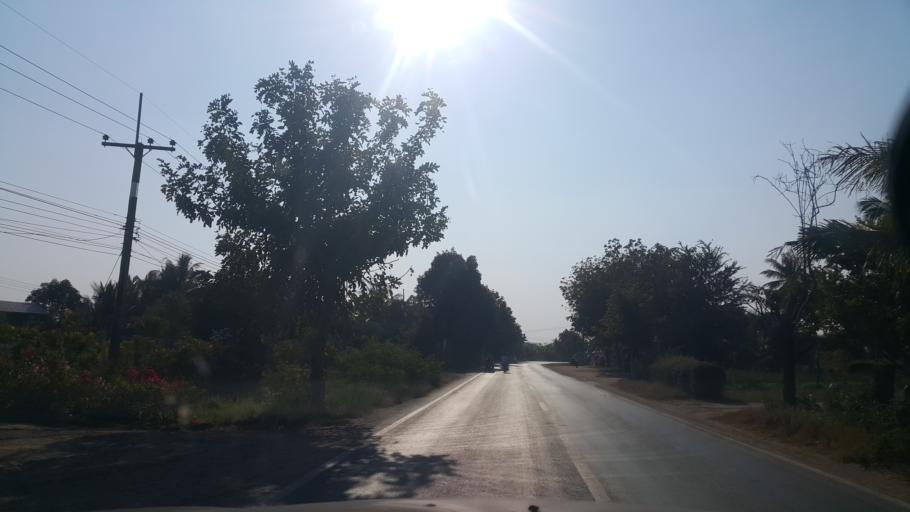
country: TH
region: Nakhon Ratchasima
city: Phimai
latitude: 15.1651
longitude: 102.3892
